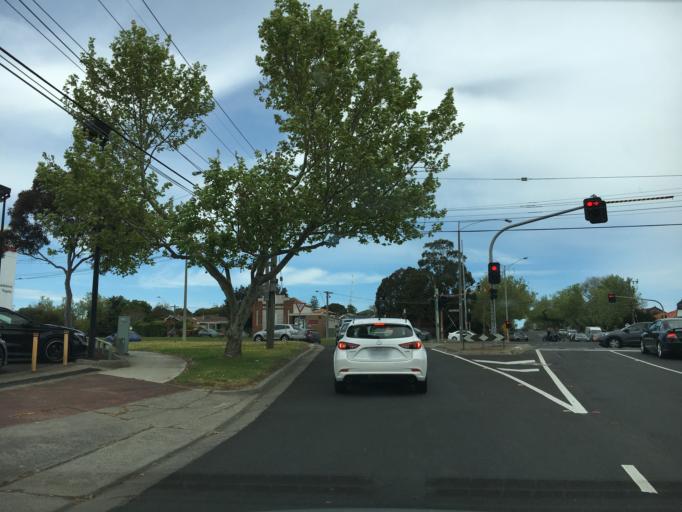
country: AU
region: Victoria
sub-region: Monash
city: Chadstone
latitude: -37.8932
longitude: 145.0935
